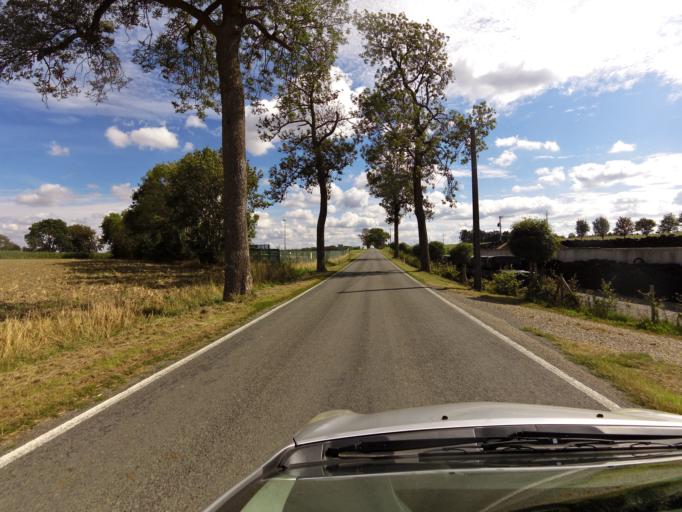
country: BE
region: Wallonia
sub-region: Province de Namur
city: Somme-Leuze
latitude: 50.3537
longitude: 5.3299
